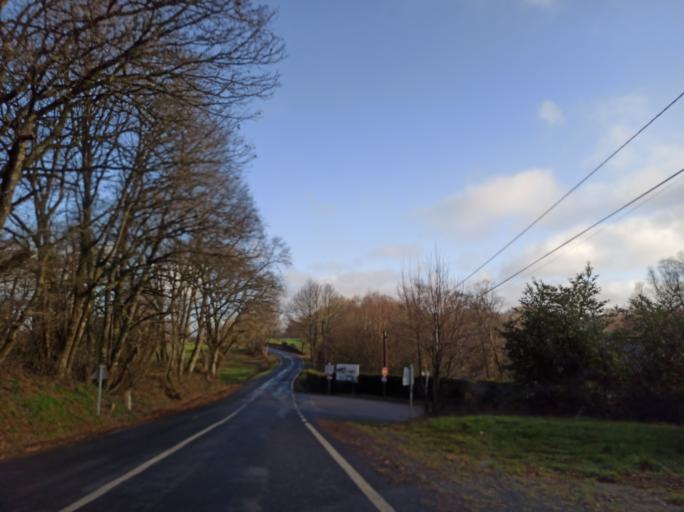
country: ES
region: Galicia
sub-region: Provincia da Coruna
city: Curtis
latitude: 43.0924
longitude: -7.9933
